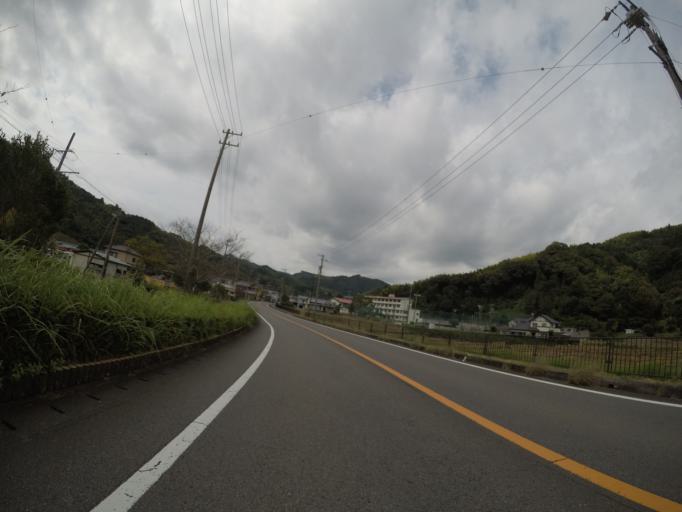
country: JP
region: Shizuoka
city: Fujieda
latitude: 34.8803
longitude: 138.2197
